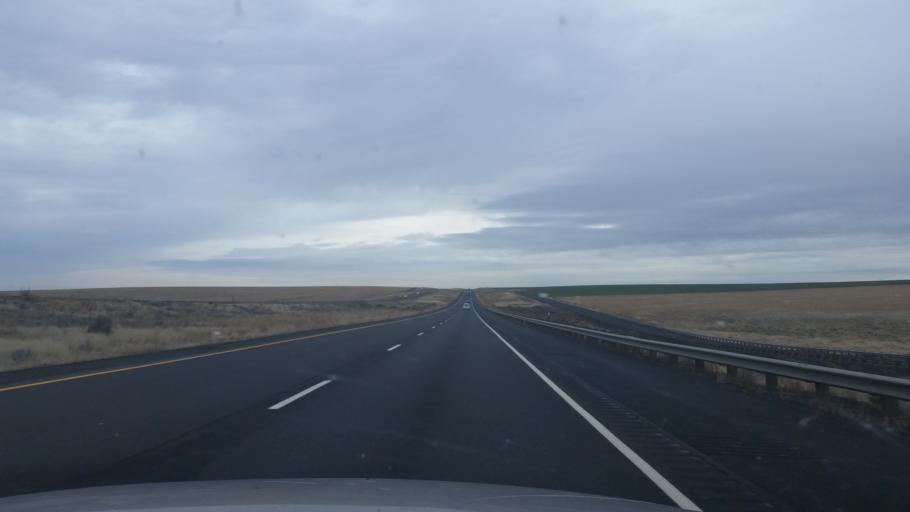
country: US
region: Washington
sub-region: Grant County
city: Warden
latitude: 47.0864
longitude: -118.7520
